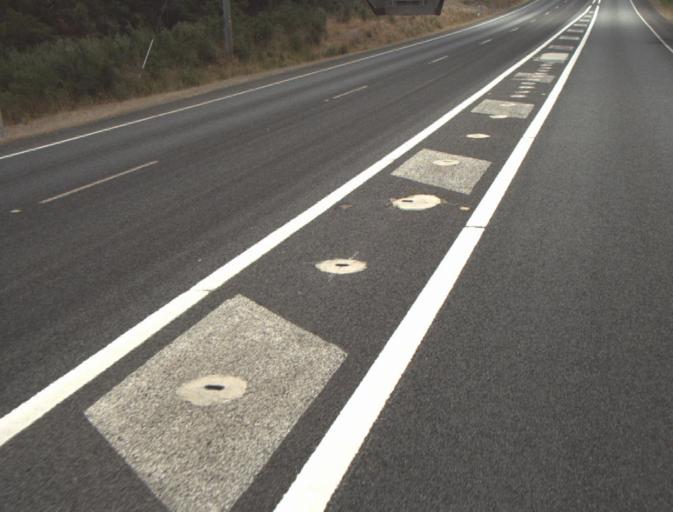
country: AU
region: Tasmania
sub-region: Launceston
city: Mayfield
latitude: -41.2893
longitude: 147.0429
